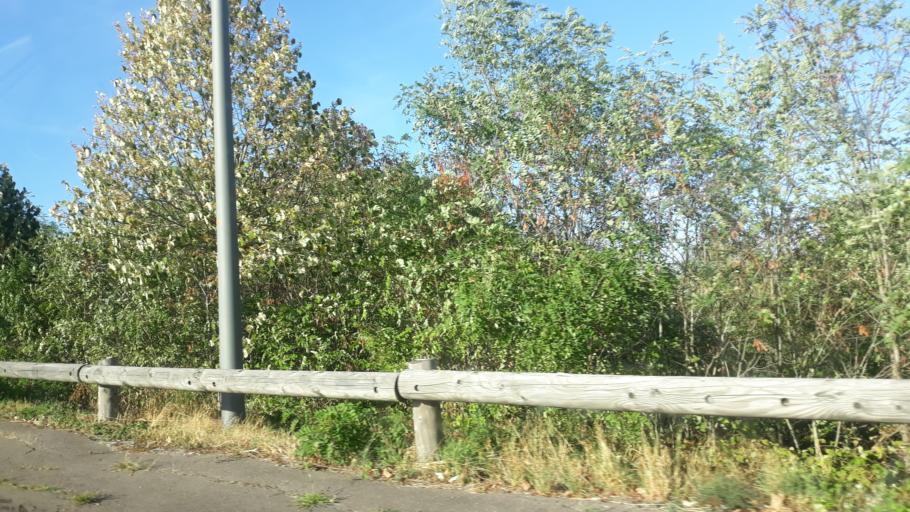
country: FR
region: Bourgogne
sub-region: Departement de Saone-et-Loire
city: Torcy
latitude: 46.7779
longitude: 4.4436
